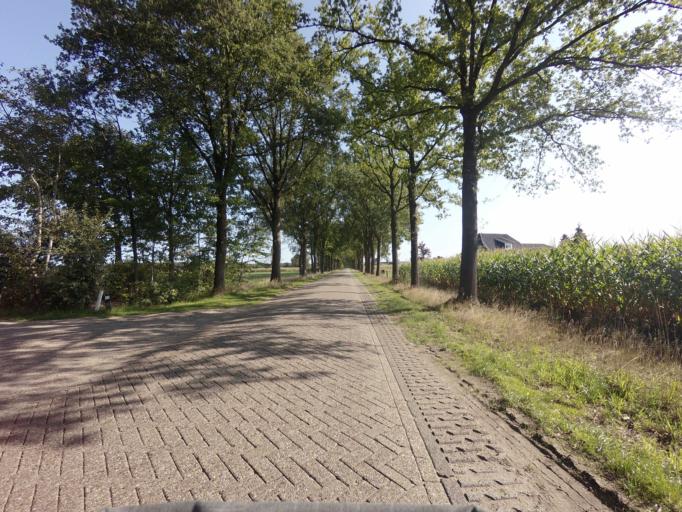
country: NL
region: Overijssel
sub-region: Gemeente Raalte
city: Raalte
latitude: 52.4199
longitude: 6.2897
